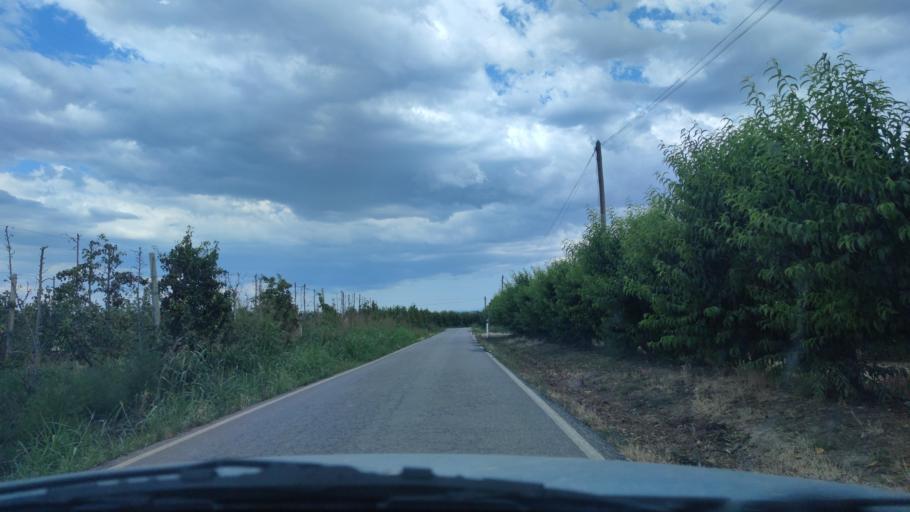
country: ES
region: Catalonia
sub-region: Provincia de Lleida
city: Lleida
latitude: 41.6251
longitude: 0.5776
